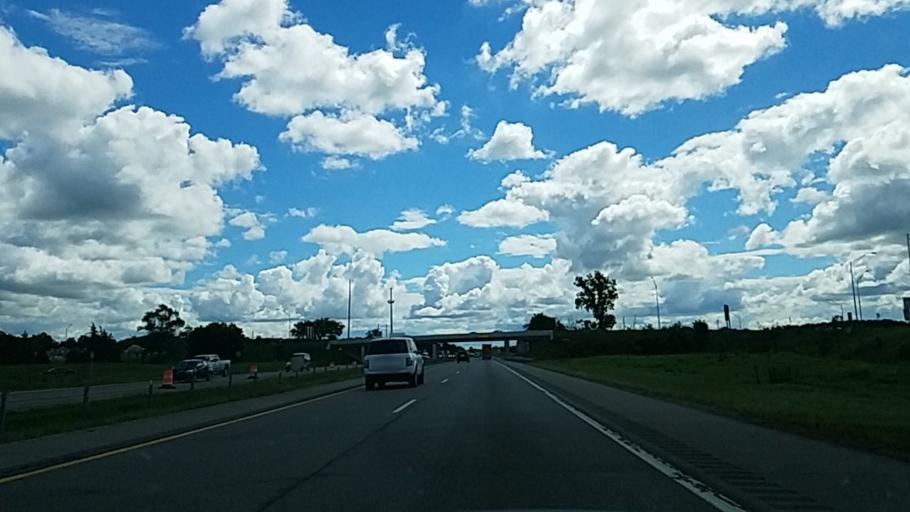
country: US
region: Michigan
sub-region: Livingston County
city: Brighton
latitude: 42.5072
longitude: -83.7583
